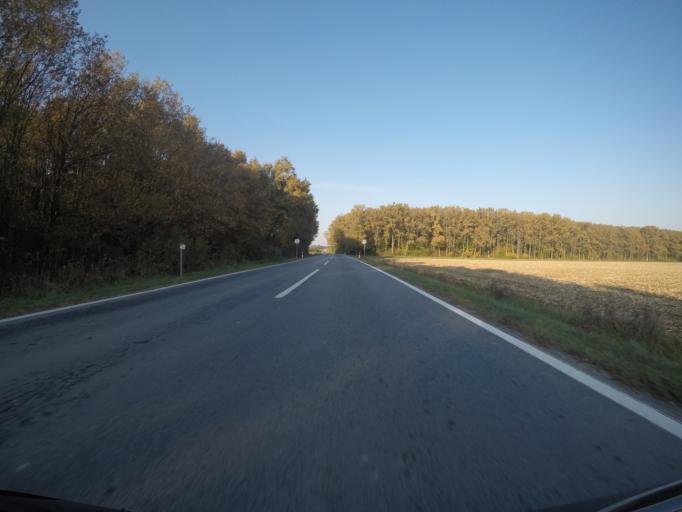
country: HR
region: Virovitick-Podravska
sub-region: Grad Virovitica
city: Virovitica
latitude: 45.8806
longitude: 17.4071
